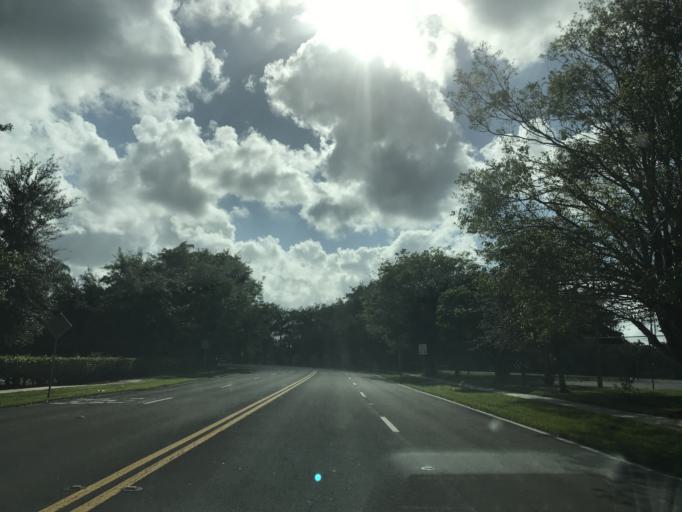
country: US
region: Florida
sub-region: Broward County
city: Coconut Creek
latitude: 26.2508
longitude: -80.1915
